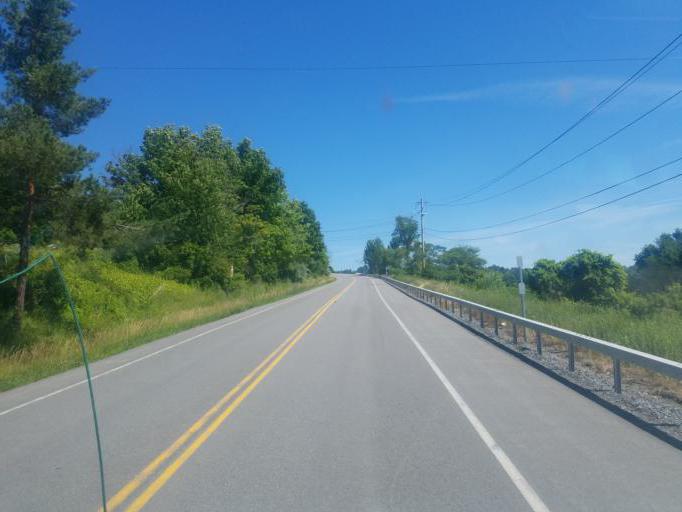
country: US
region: New York
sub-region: Ontario County
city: Naples
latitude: 42.7140
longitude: -77.2759
